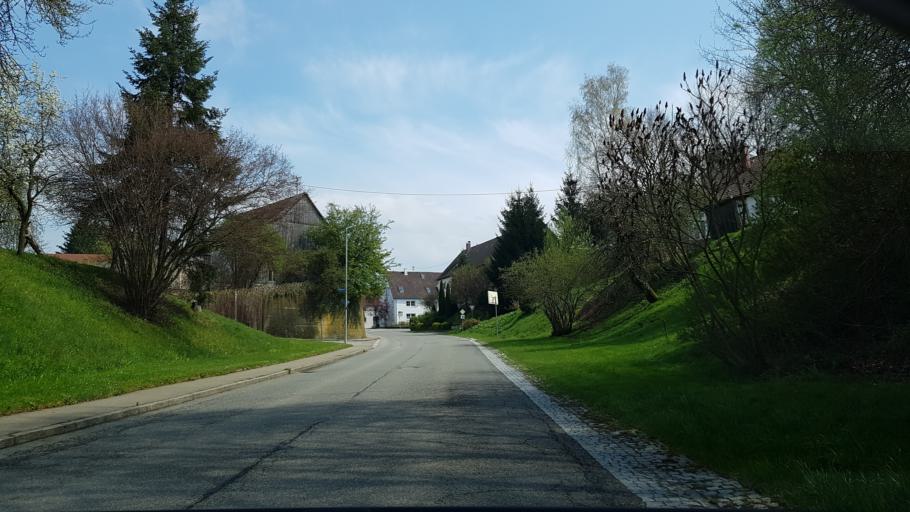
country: DE
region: Baden-Wuerttemberg
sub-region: Tuebingen Region
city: Wain
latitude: 48.2123
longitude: 10.0185
